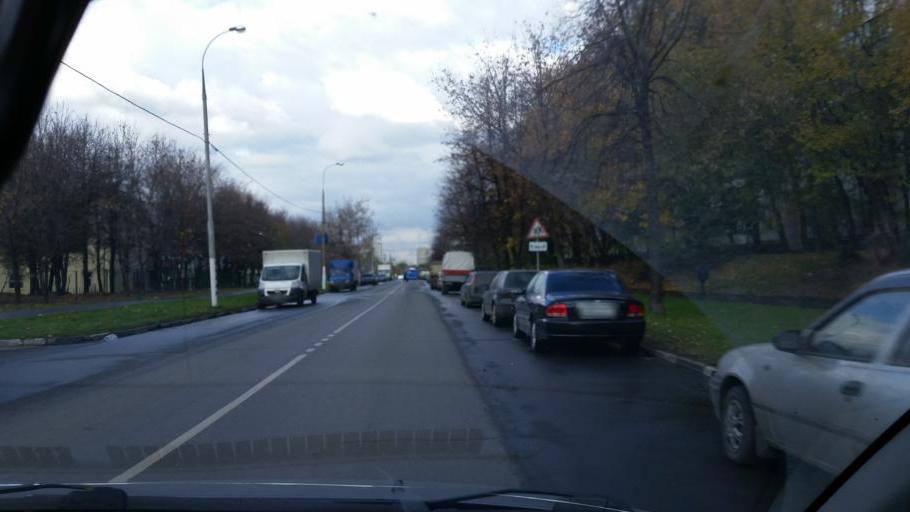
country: RU
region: Moscow
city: Chertanovo Yuzhnoye
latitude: 55.5975
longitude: 37.6066
